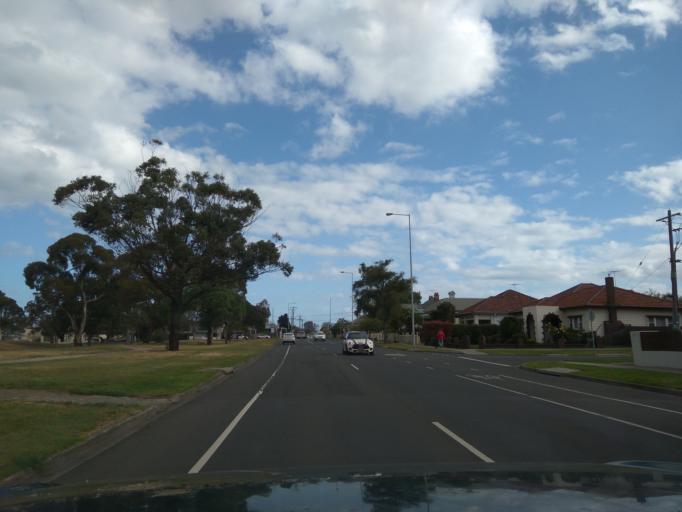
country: AU
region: Victoria
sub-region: Hobsons Bay
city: Newport
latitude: -37.8436
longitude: 144.8926
